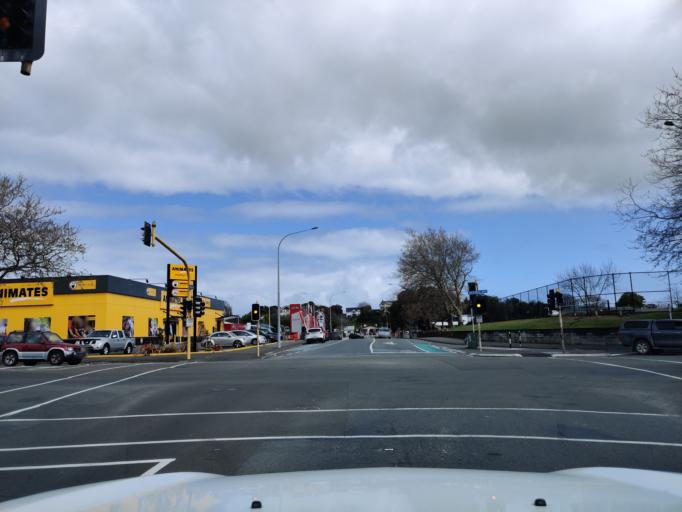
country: NZ
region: Manawatu-Wanganui
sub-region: Wanganui District
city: Wanganui
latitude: -39.9278
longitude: 175.0437
